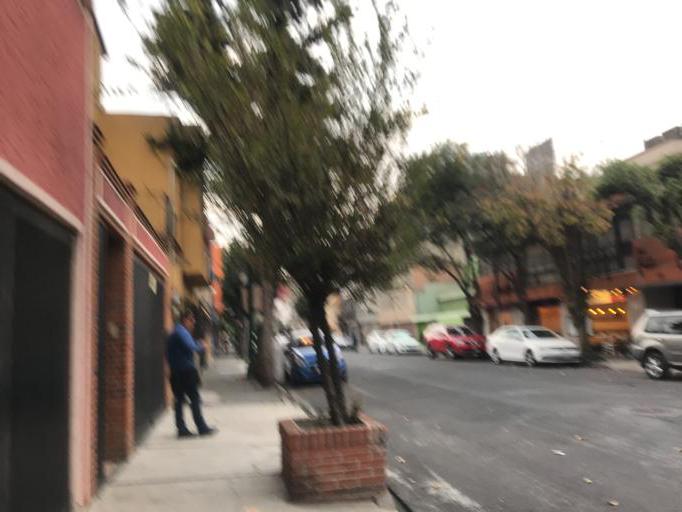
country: MX
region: Mexico City
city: Colonia del Valle
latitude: 19.3799
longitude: -99.1575
